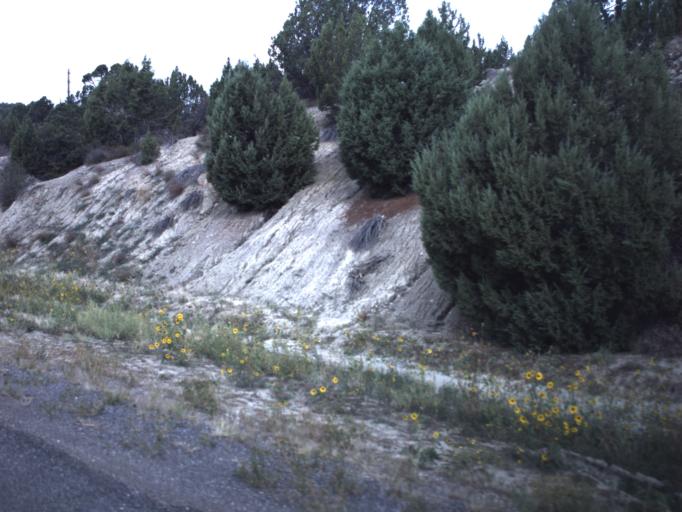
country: US
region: Utah
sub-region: Washington County
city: Hildale
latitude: 37.2620
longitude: -112.7896
